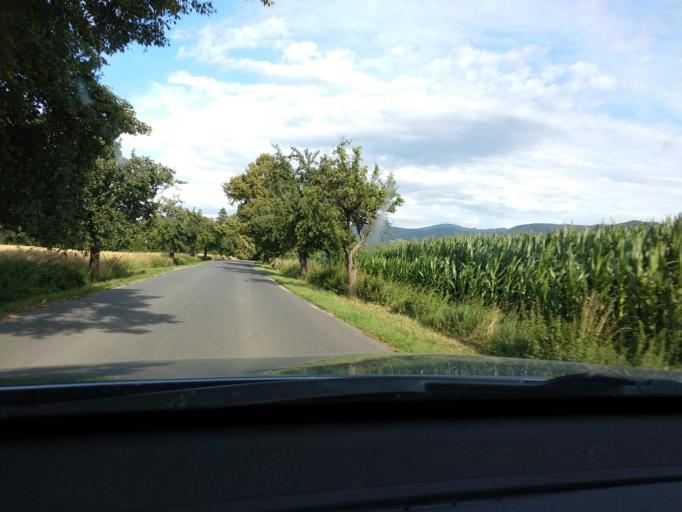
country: SK
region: Zilinsky
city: Ruzomberok
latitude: 49.0633
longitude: 19.3323
